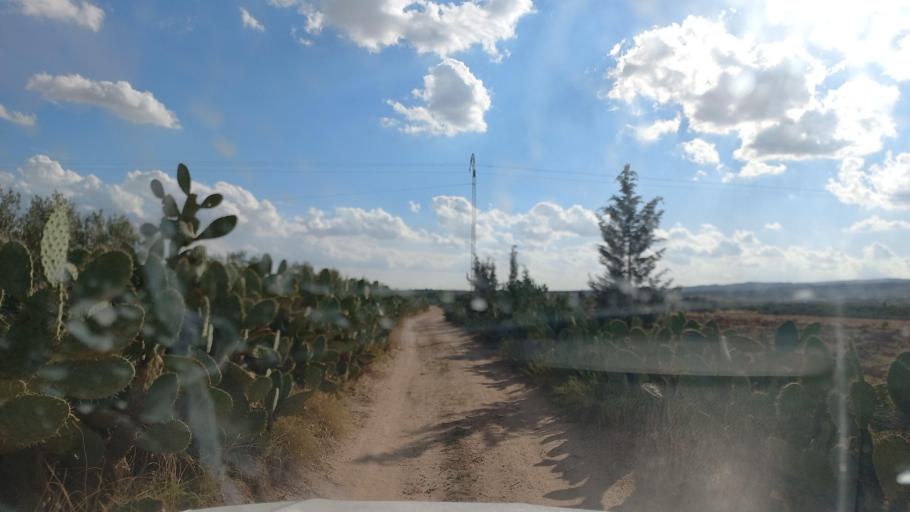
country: TN
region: Al Qasrayn
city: Sbiba
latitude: 35.3859
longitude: 9.0387
